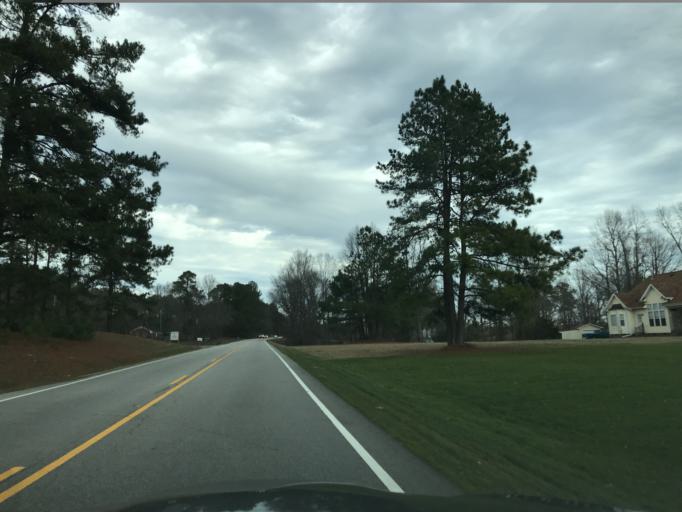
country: US
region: North Carolina
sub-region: Franklin County
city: Louisburg
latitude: 36.0298
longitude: -78.3534
